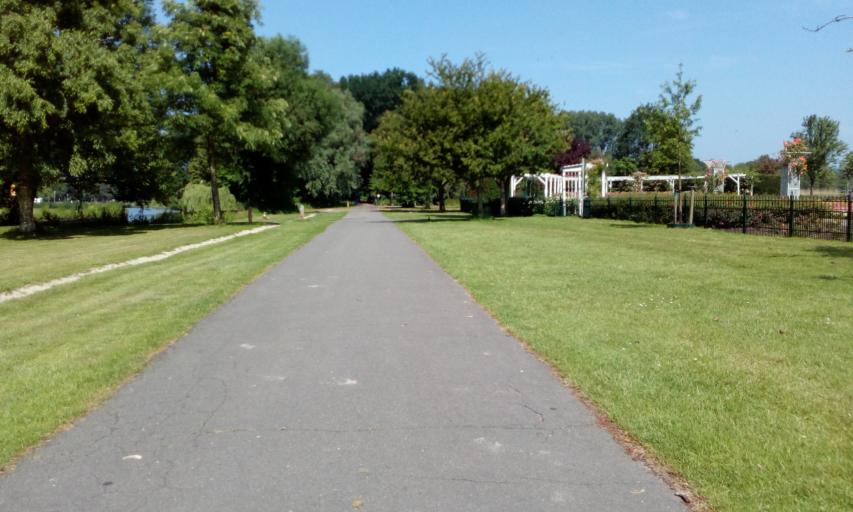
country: NL
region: South Holland
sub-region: Gemeente Den Haag
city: The Hague
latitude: 52.0563
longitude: 4.2873
